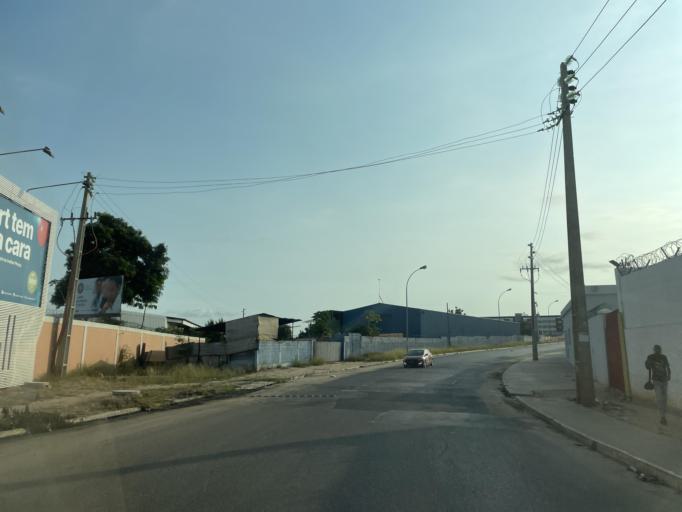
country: AO
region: Luanda
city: Luanda
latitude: -8.9193
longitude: 13.2049
